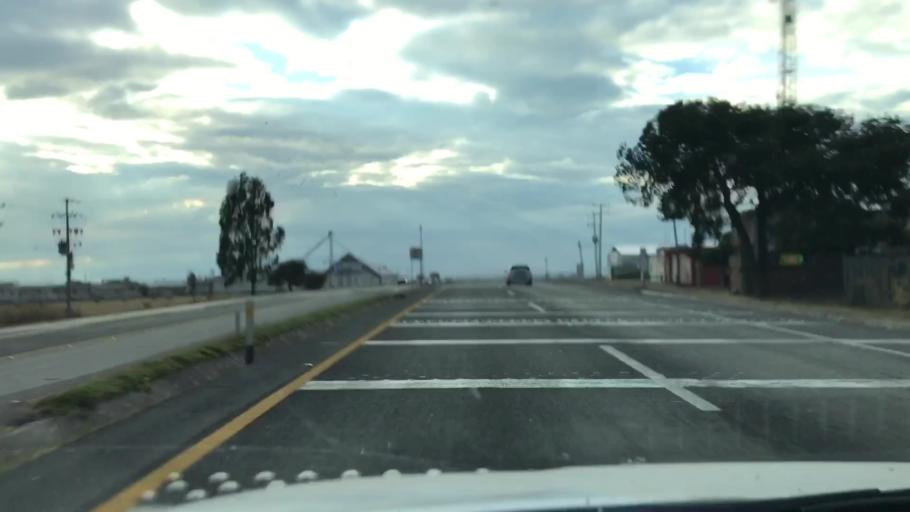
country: MX
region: Guanajuato
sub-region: Penjamo
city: Mezquite de Luna
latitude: 20.3793
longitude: -101.8360
